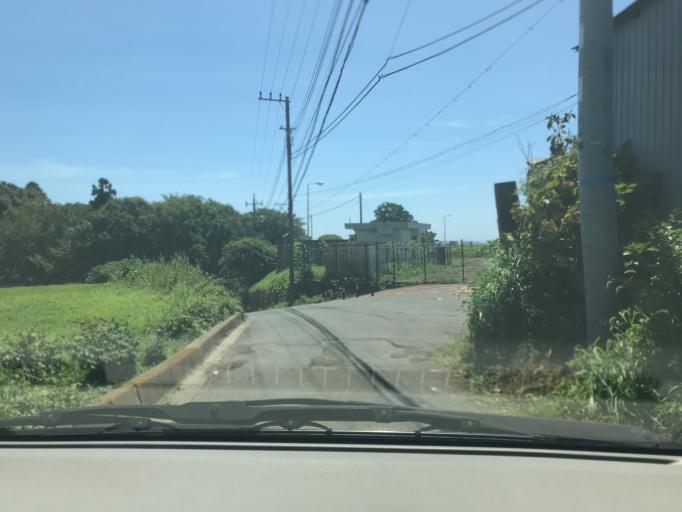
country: JP
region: Kanagawa
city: Fujisawa
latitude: 35.3510
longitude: 139.4407
